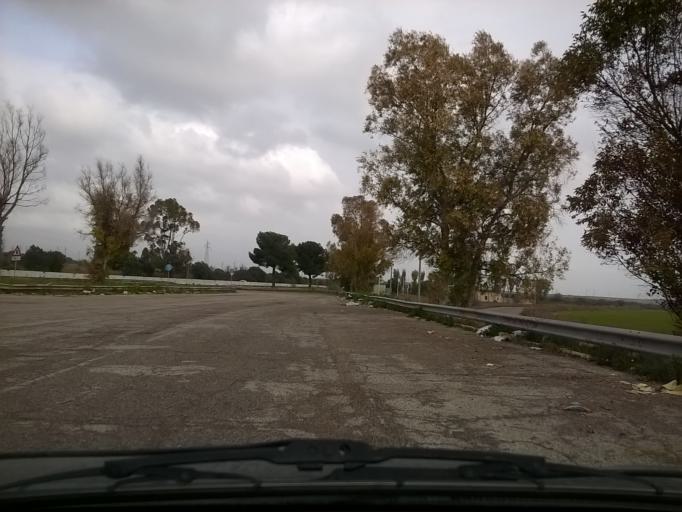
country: IT
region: Apulia
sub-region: Provincia di Taranto
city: Paolo VI
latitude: 40.5140
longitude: 17.3079
